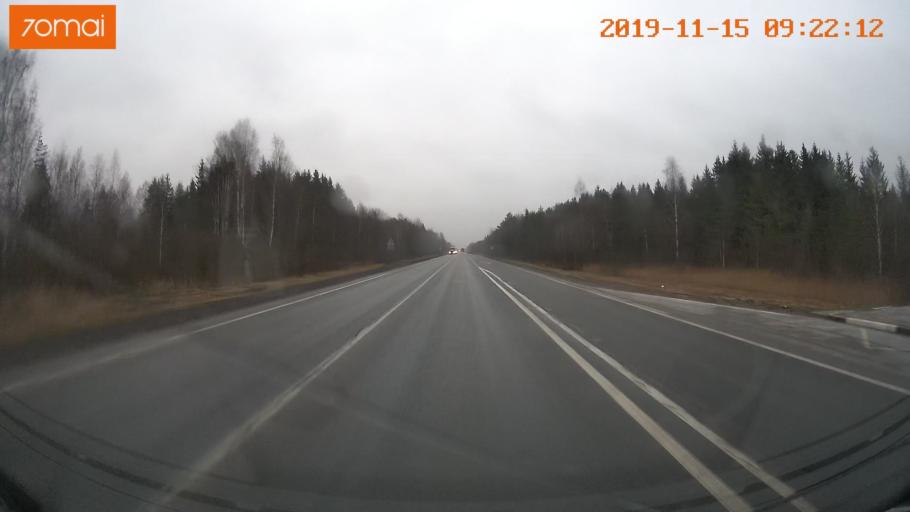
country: RU
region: Vologda
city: Tonshalovo
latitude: 59.2971
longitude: 38.0840
